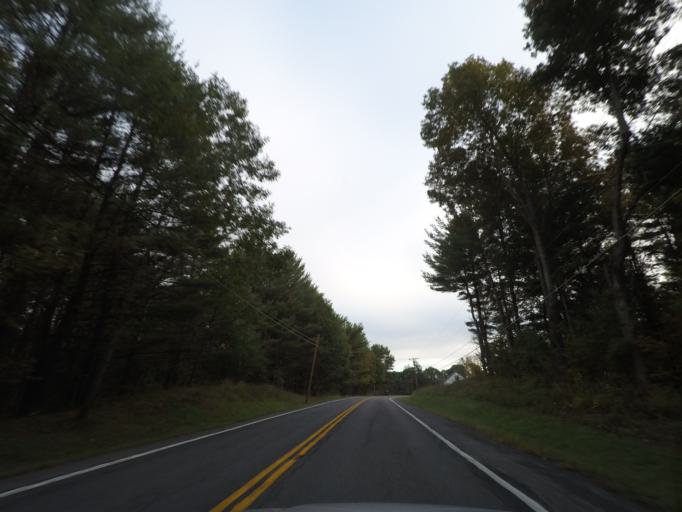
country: US
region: New York
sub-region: Rensselaer County
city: Nassau
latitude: 42.5745
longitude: -73.6246
